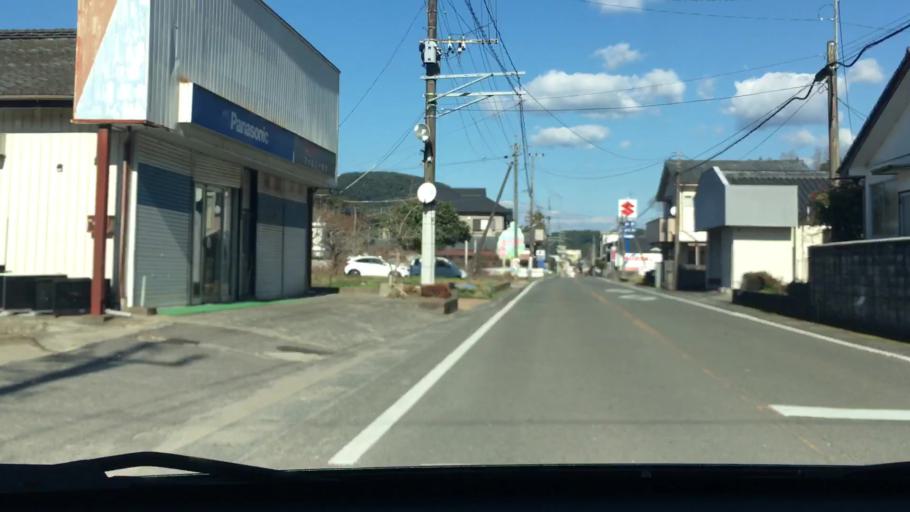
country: JP
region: Kagoshima
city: Satsumasendai
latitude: 31.7846
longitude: 130.4020
